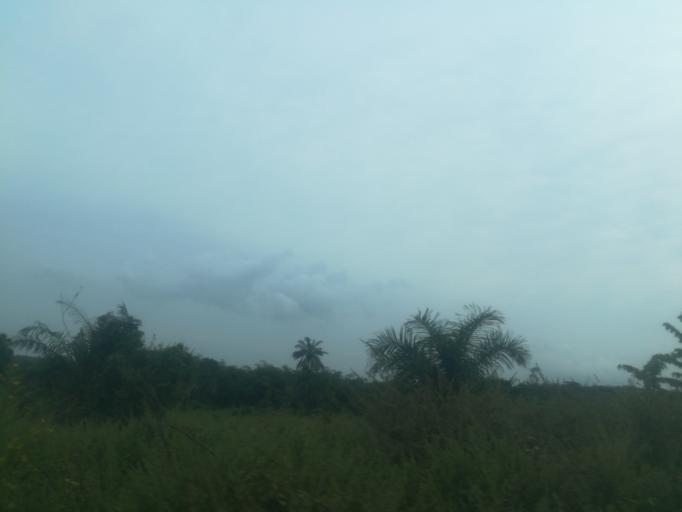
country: NG
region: Ogun
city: Ayetoro
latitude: 7.2151
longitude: 3.1802
